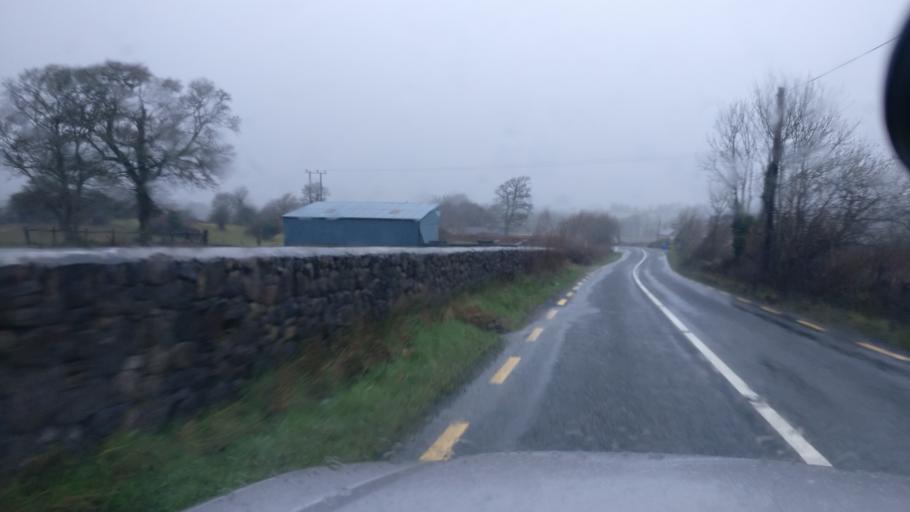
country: IE
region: Connaught
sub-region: County Galway
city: Loughrea
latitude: 53.1472
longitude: -8.4727
